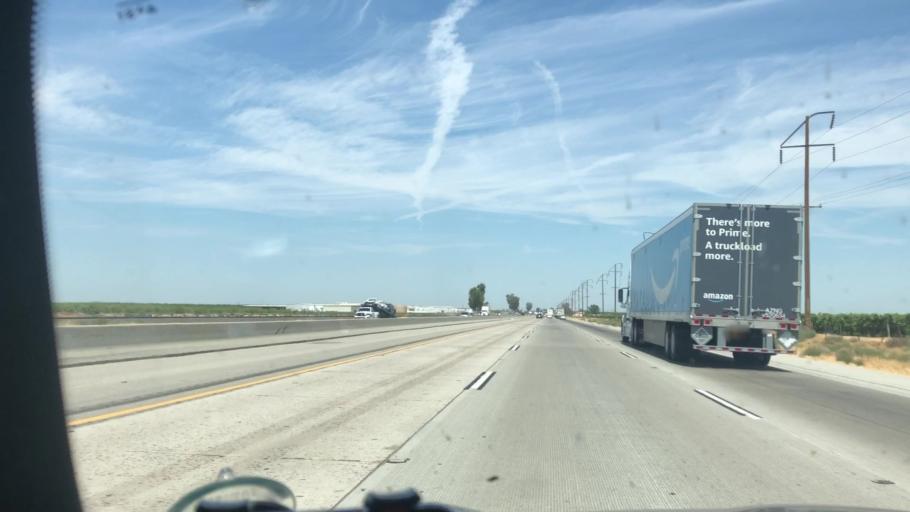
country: US
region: California
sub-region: Kern County
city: Rosedale
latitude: 35.4789
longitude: -119.1367
